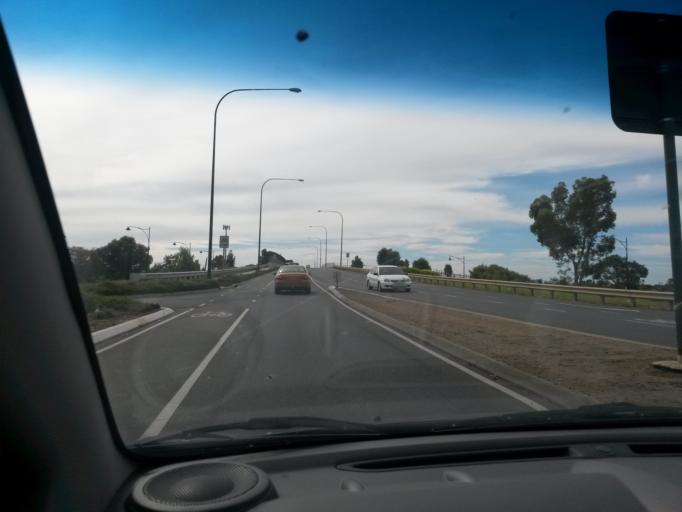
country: AU
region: South Australia
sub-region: Salisbury
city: Ingle Farm
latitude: -34.8048
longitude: 138.6149
